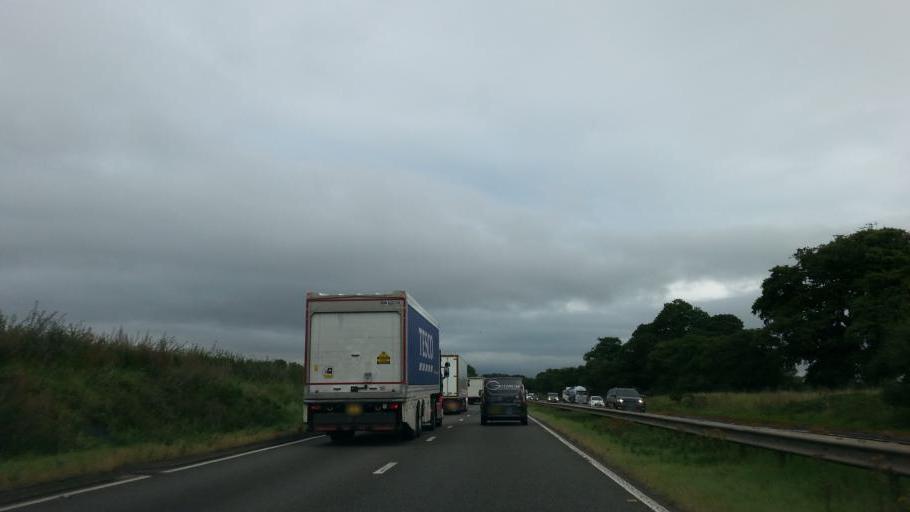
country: GB
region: England
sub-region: Nottinghamshire
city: Babworth
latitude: 53.3349
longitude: -1.0284
